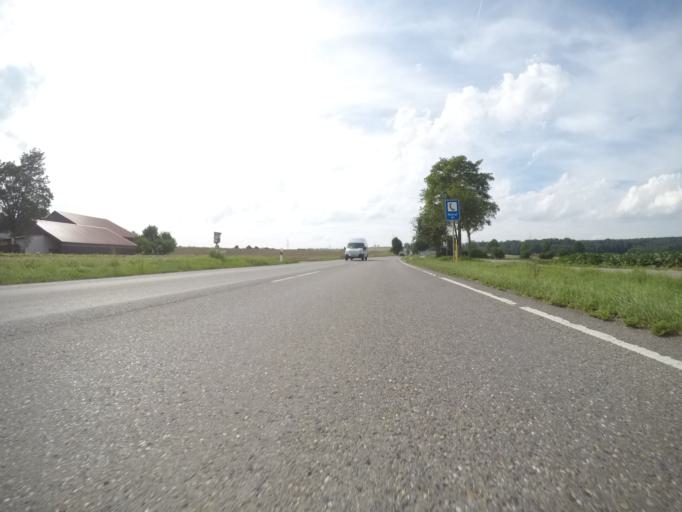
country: DE
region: Baden-Wuerttemberg
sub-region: Regierungsbezirk Stuttgart
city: Hemmingen
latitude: 48.8408
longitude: 9.0120
